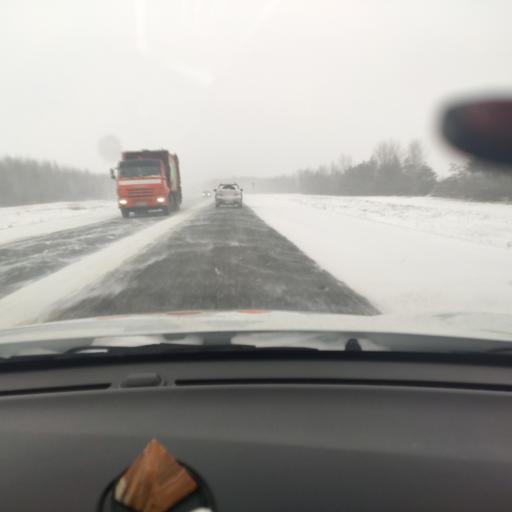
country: RU
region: Tatarstan
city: Verkhniy Uslon
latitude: 55.6691
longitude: 48.8658
